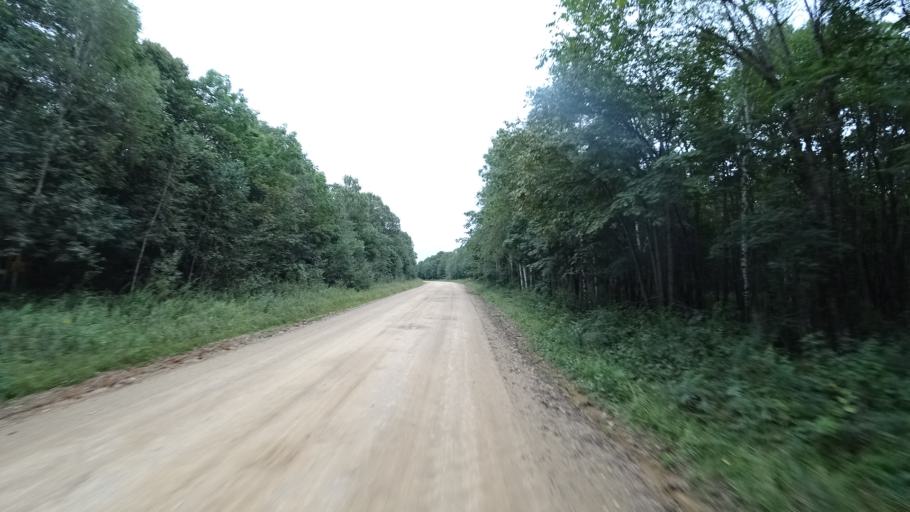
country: RU
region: Primorskiy
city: Rettikhovka
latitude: 44.1838
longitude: 132.8199
